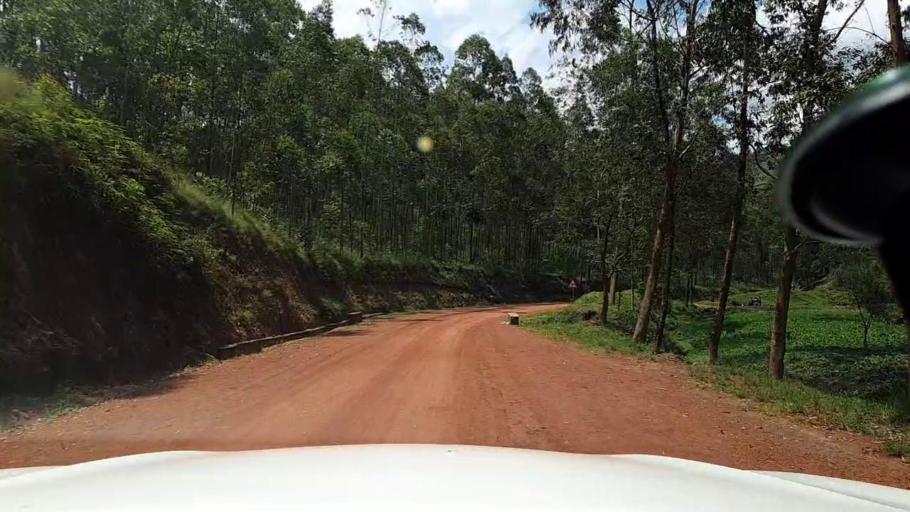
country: RW
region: Northern Province
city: Byumba
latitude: -1.6999
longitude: 29.8346
